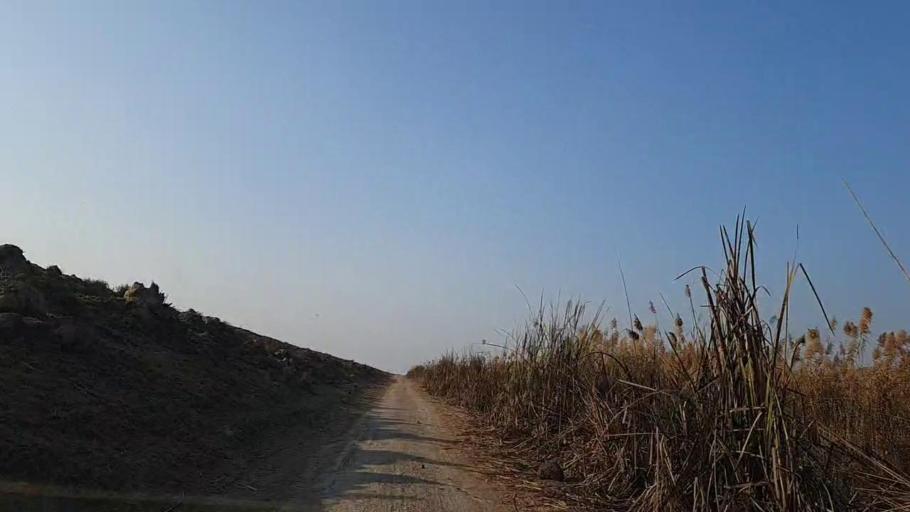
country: PK
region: Sindh
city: Sakrand
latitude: 26.0987
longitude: 68.3690
